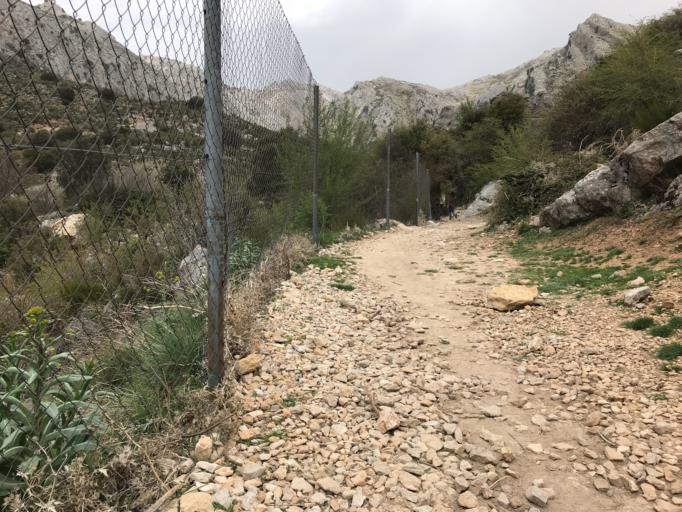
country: ES
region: Andalusia
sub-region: Provincia de Granada
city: Castril
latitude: 37.8956
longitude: -2.7476
